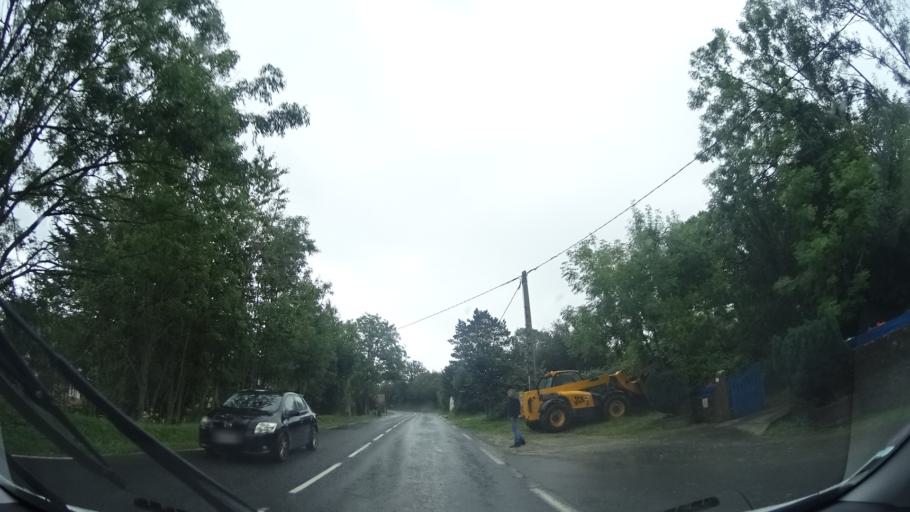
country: FR
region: Lower Normandy
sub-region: Departement de la Manche
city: Beaumont-Hague
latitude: 49.6076
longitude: -1.7905
